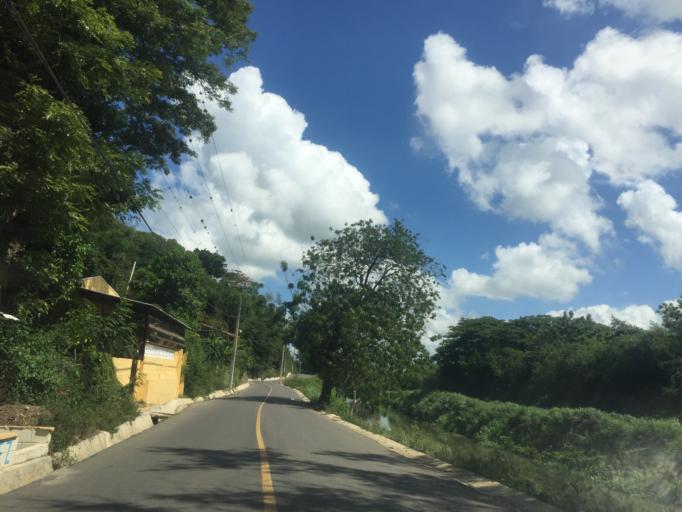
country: DO
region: Santiago
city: Santiago de los Caballeros
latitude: 19.4496
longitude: -70.7540
